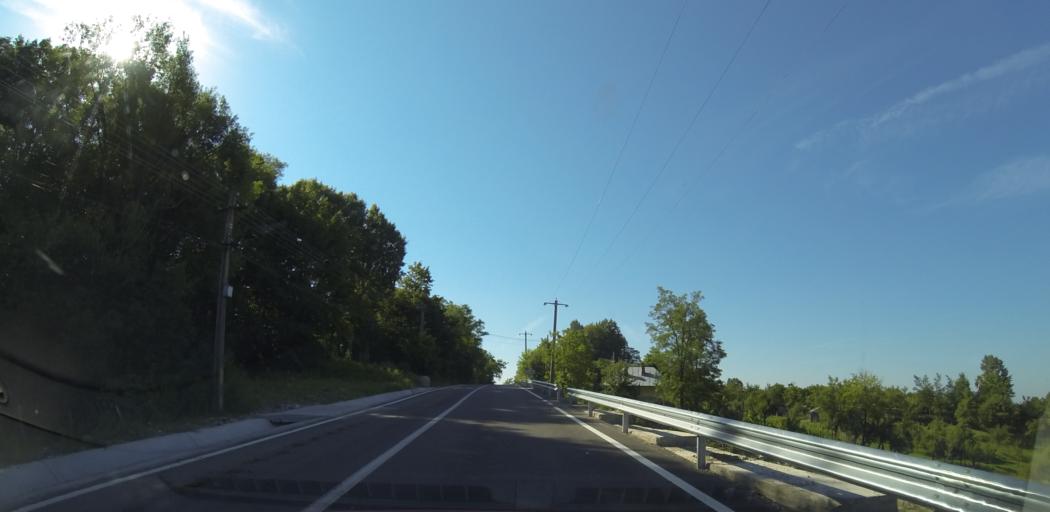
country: RO
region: Valcea
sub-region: Comuna Vaideeni
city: Vaideeni
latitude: 45.1687
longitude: 23.8862
